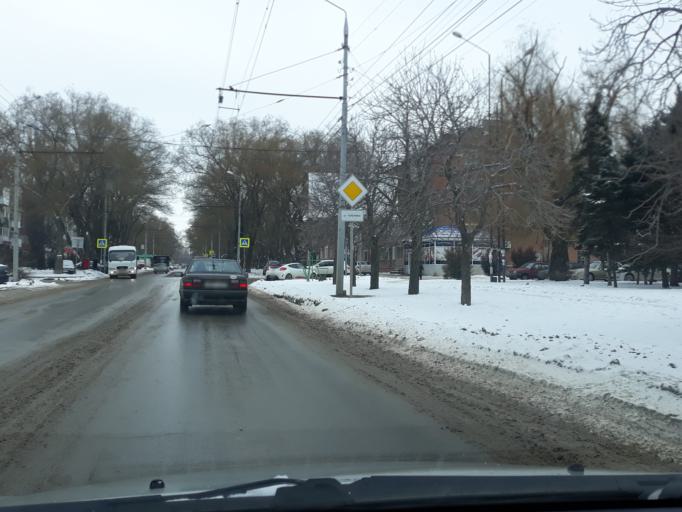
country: RU
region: Rostov
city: Taganrog
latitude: 47.2536
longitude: 38.9179
